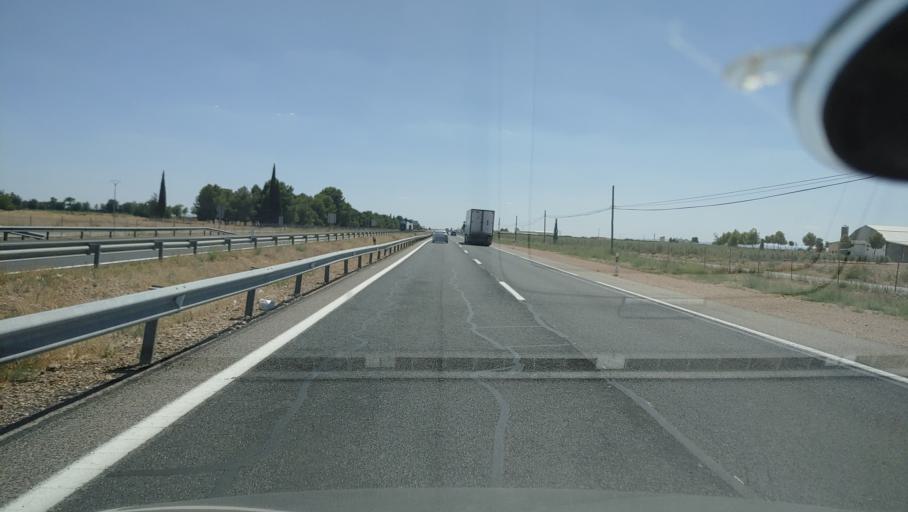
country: ES
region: Castille-La Mancha
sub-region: Provincia de Ciudad Real
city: Manzanares
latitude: 39.1204
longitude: -3.3779
